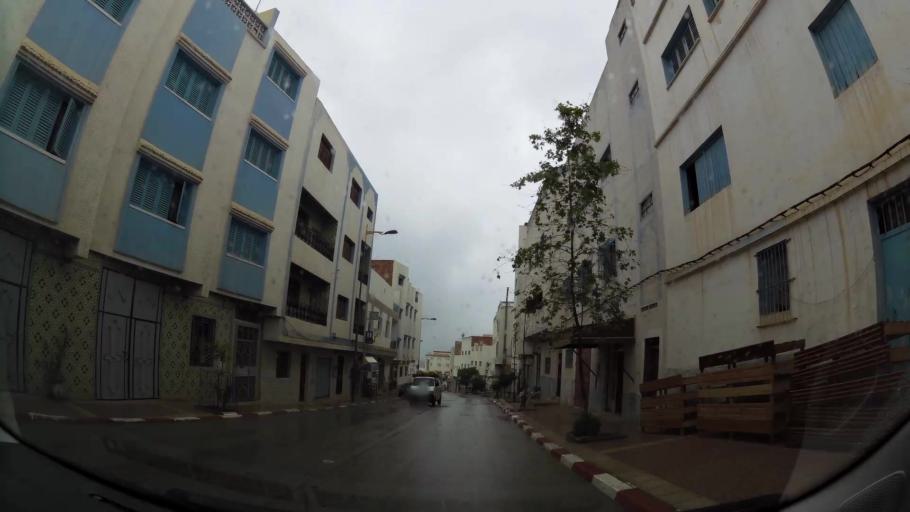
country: MA
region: Taza-Al Hoceima-Taounate
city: Imzourene
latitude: 35.1525
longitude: -3.8489
